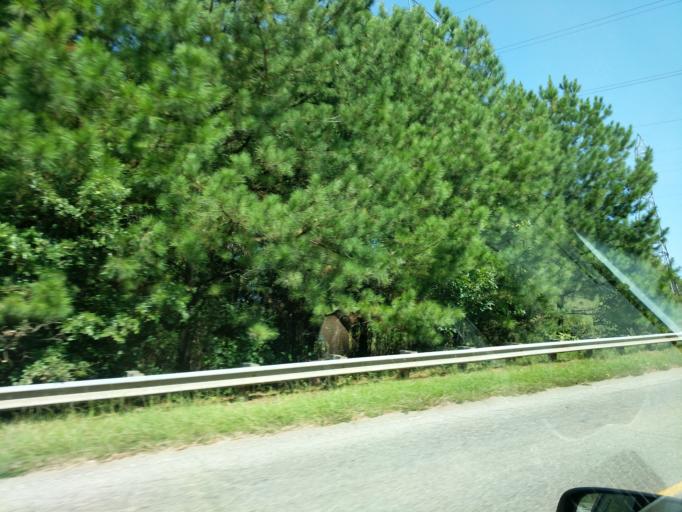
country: US
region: South Carolina
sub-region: Spartanburg County
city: Duncan
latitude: 34.9056
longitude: -82.1157
